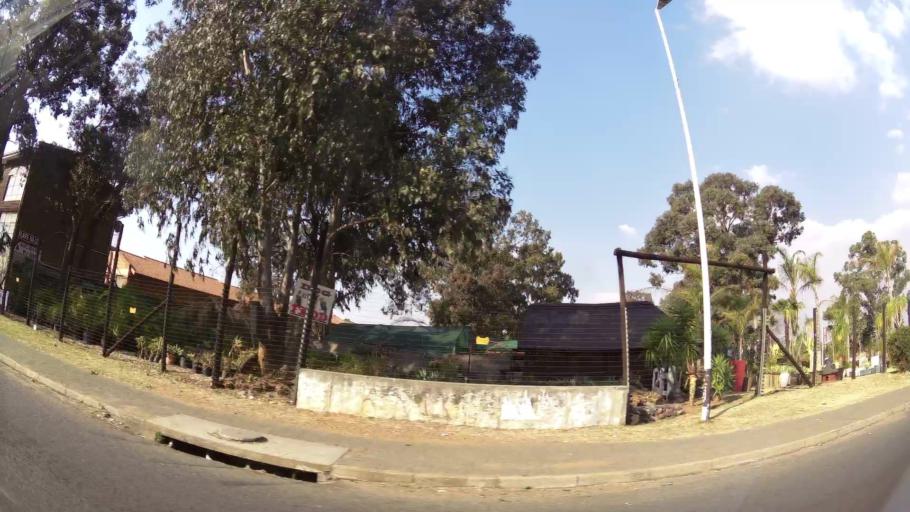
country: ZA
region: Gauteng
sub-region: Ekurhuleni Metropolitan Municipality
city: Boksburg
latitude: -26.2110
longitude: 28.2537
